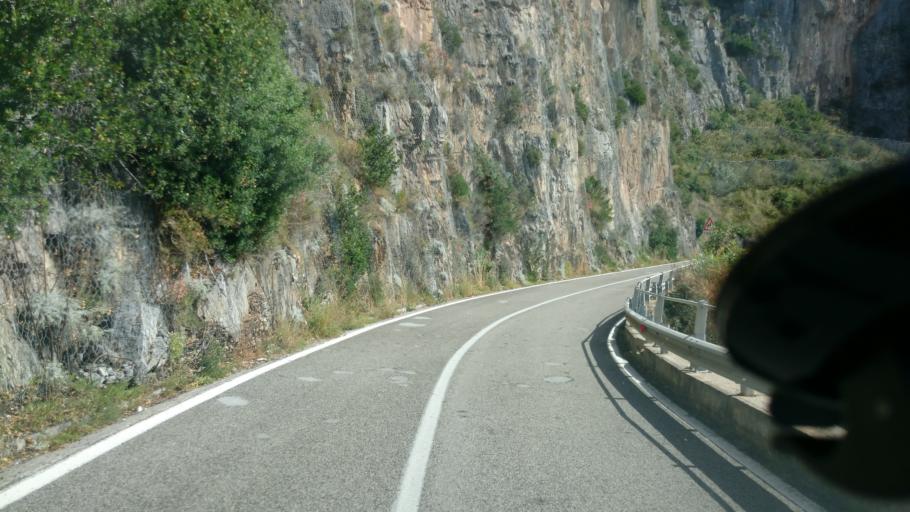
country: IT
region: Campania
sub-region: Provincia di Salerno
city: Sapri
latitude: 40.0410
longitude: 15.6506
